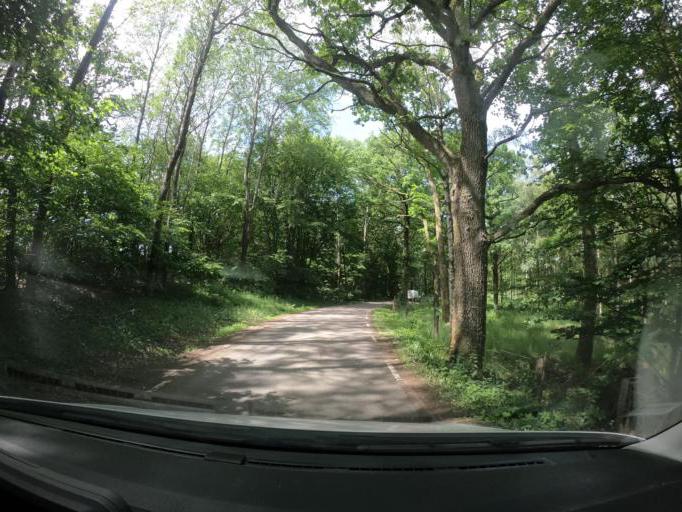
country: SE
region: Skane
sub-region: Orkelljunga Kommun
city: OErkelljunga
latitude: 56.2284
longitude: 13.2425
